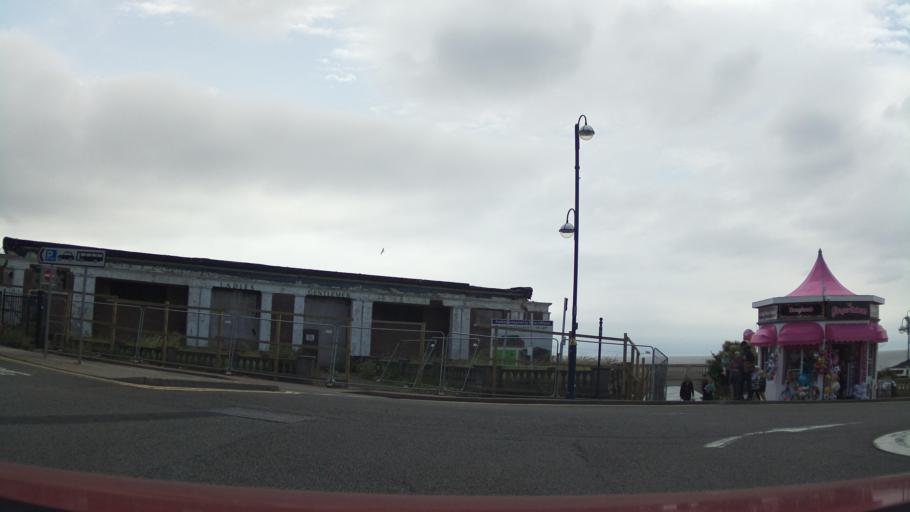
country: GB
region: Wales
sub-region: Vale of Glamorgan
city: Barry
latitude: 51.3914
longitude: -3.2723
